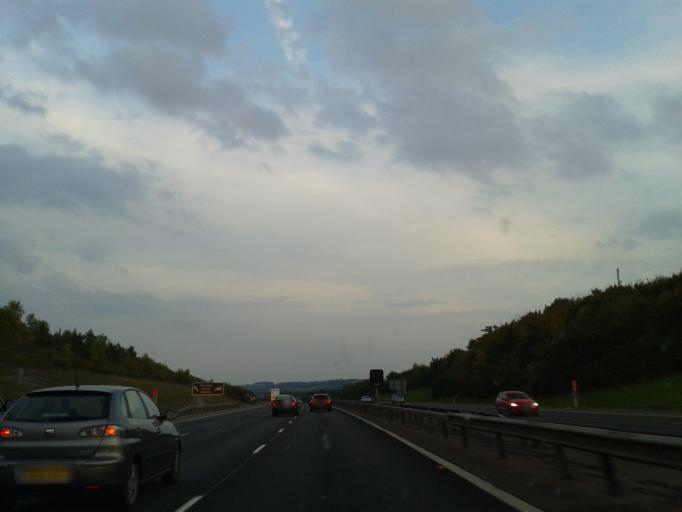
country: GB
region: England
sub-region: Warwickshire
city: Harbury
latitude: 52.1969
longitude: -1.4669
